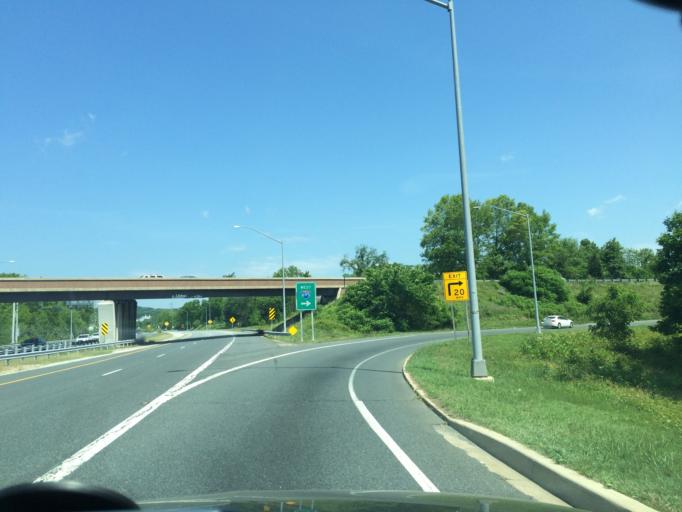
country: US
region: Maryland
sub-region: Baltimore County
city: Mays Chapel
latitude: 39.4123
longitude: -76.6640
